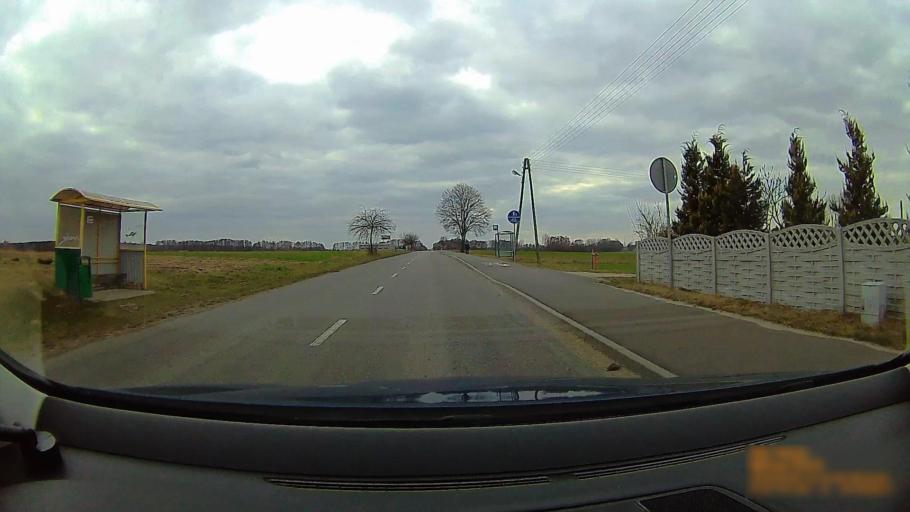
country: PL
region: Greater Poland Voivodeship
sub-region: Powiat koninski
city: Rzgow Pierwszy
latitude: 52.1671
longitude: 18.0795
